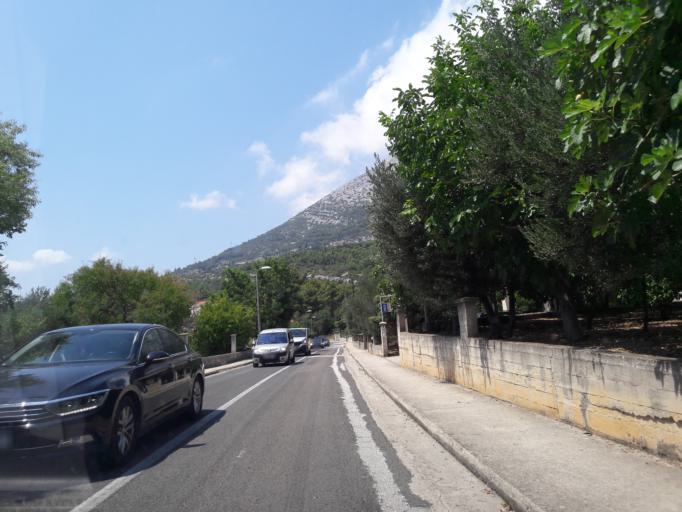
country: HR
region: Dubrovacko-Neretvanska
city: Orebic
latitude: 42.9759
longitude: 17.1740
